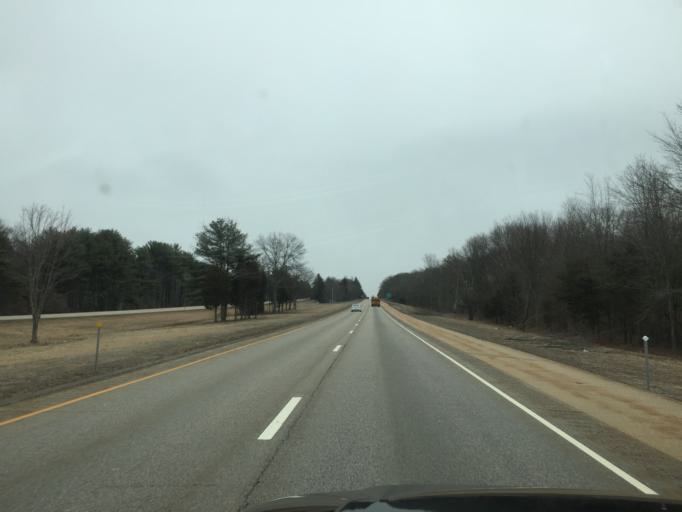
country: US
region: Connecticut
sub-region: New London County
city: Colchester
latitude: 41.5656
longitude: -72.2375
